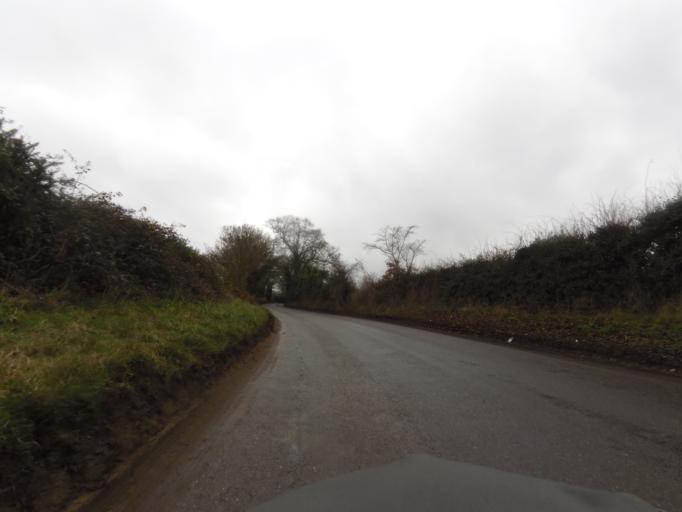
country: GB
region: England
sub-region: Norfolk
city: Briston
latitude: 52.8706
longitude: 1.0746
